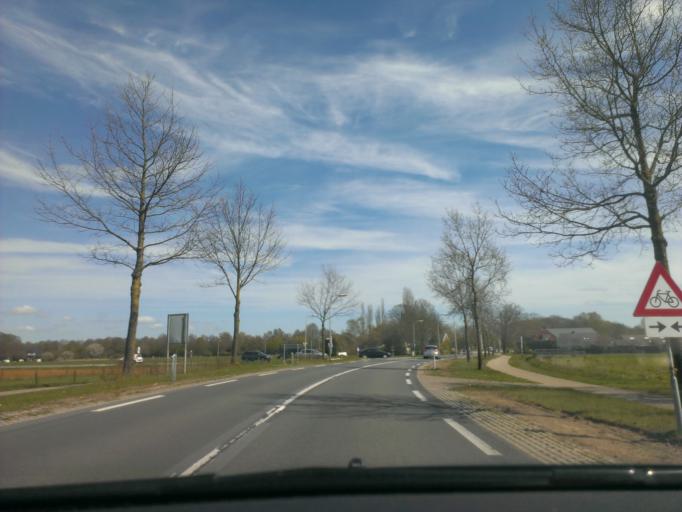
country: NL
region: Overijssel
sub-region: Gemeente Raalte
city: Raalte
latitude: 52.3878
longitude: 6.2559
